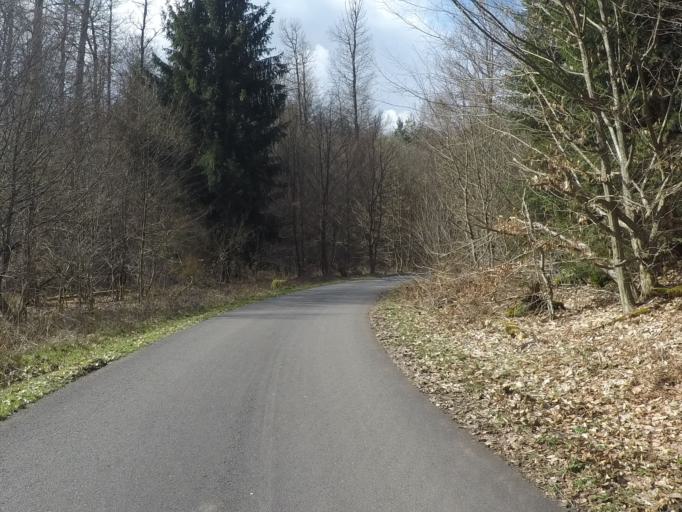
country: DE
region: Rheinland-Pfalz
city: Munchweiler an der Rodalbe
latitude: 49.2098
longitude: 7.7240
